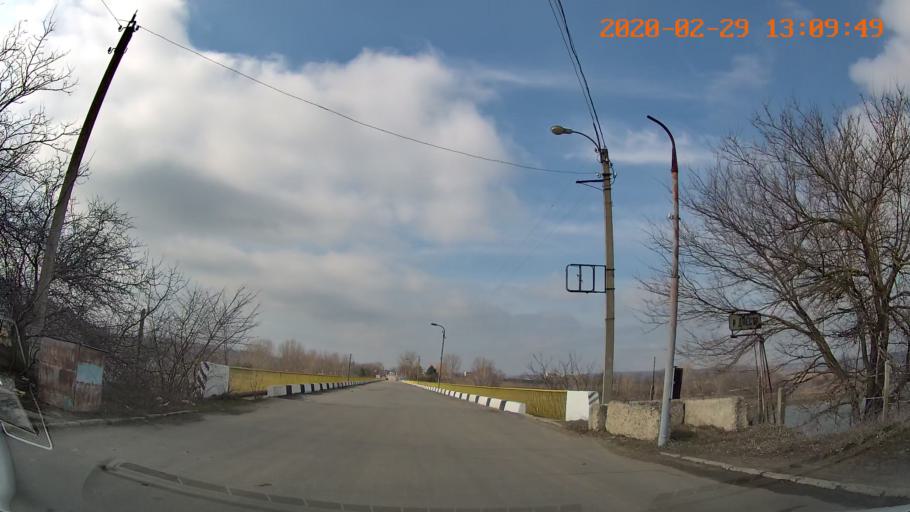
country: MD
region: Telenesti
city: Camenca
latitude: 48.0114
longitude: 28.7030
